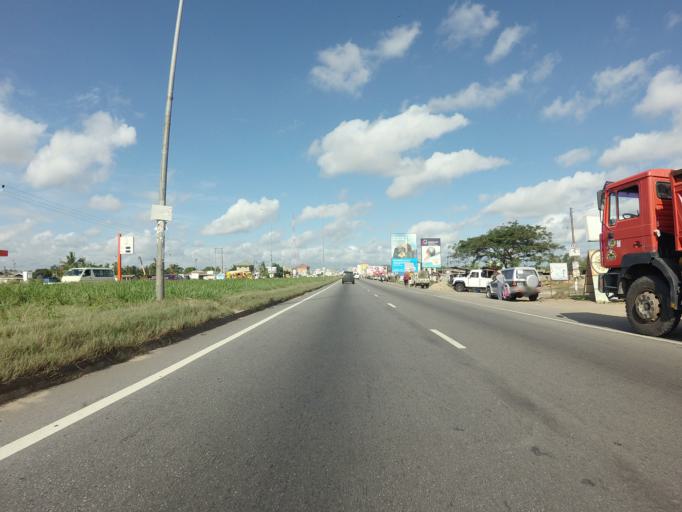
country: GH
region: Central
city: Kasoa
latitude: 5.5357
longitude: -0.4137
